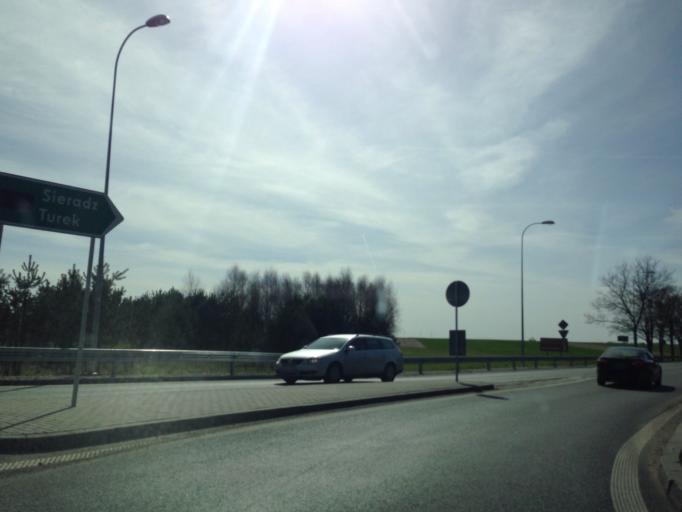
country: PL
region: Lodz Voivodeship
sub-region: Powiat sieradzki
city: Sieradz
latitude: 51.6029
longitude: 18.8117
